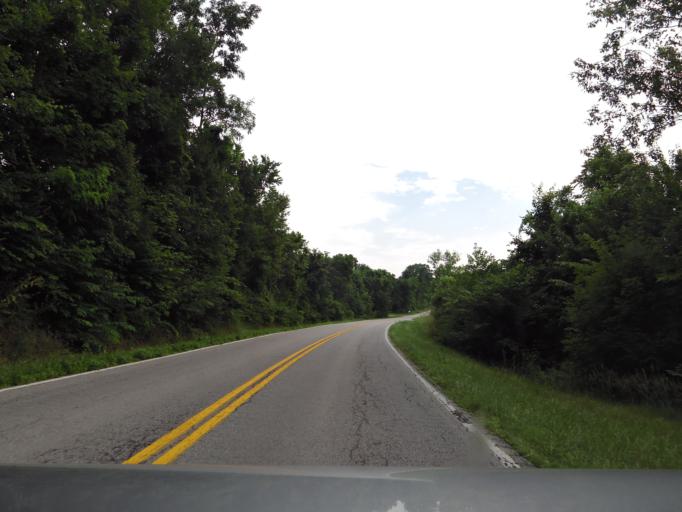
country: US
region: Kentucky
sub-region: Harrison County
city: Cynthiana
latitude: 38.4680
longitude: -84.2384
